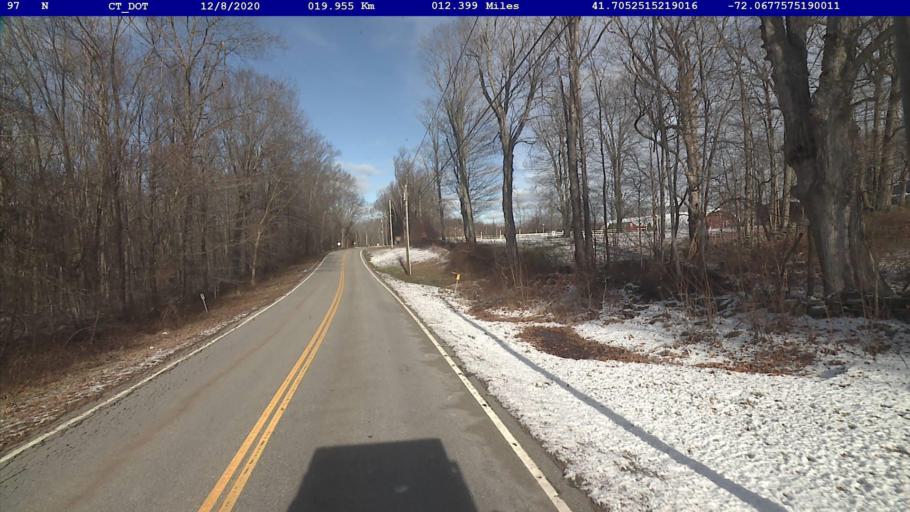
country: US
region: Connecticut
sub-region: Windham County
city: Windham
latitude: 41.7053
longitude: -72.0678
